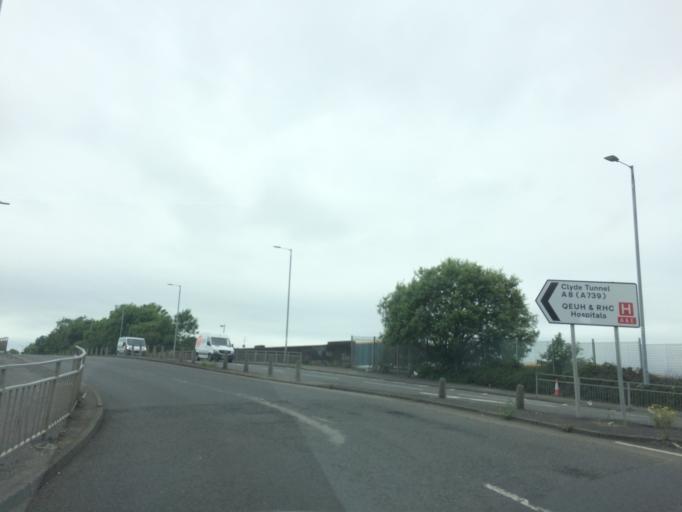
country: GB
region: Scotland
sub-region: East Renfrewshire
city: Giffnock
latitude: 55.8538
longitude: -4.3184
